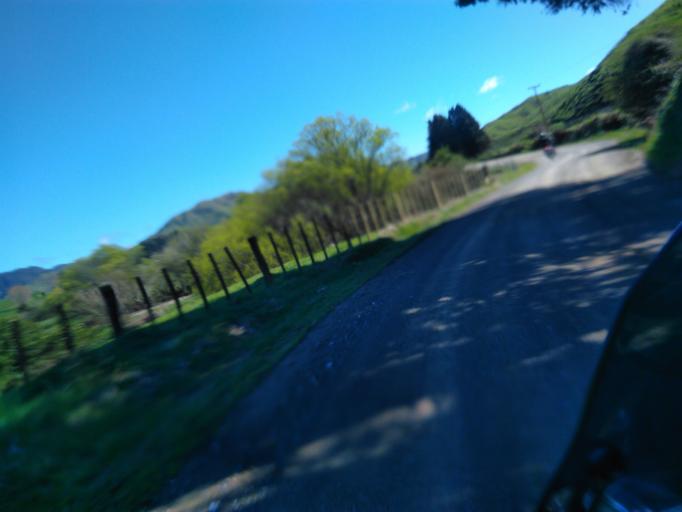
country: NZ
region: Bay of Plenty
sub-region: Opotiki District
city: Opotiki
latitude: -38.2870
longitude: 177.5437
